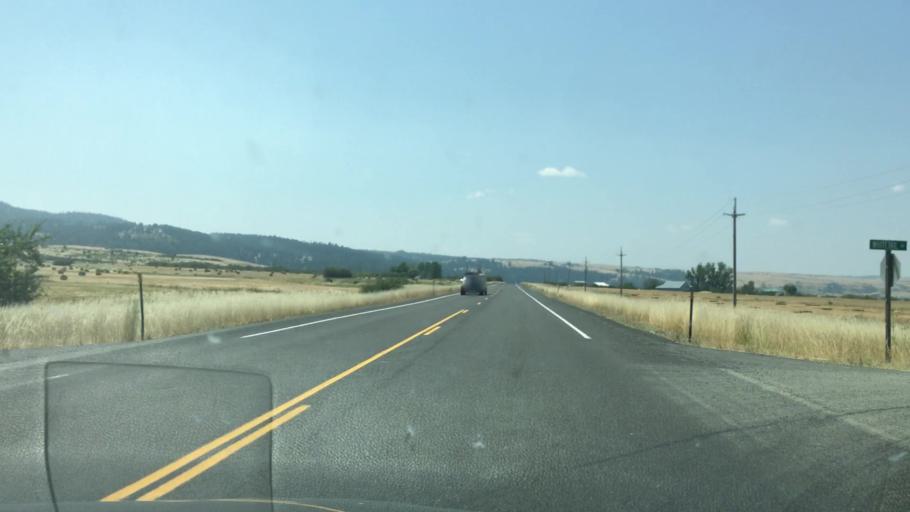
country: US
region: Idaho
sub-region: Idaho County
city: Grangeville
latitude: 45.9030
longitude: -116.1765
